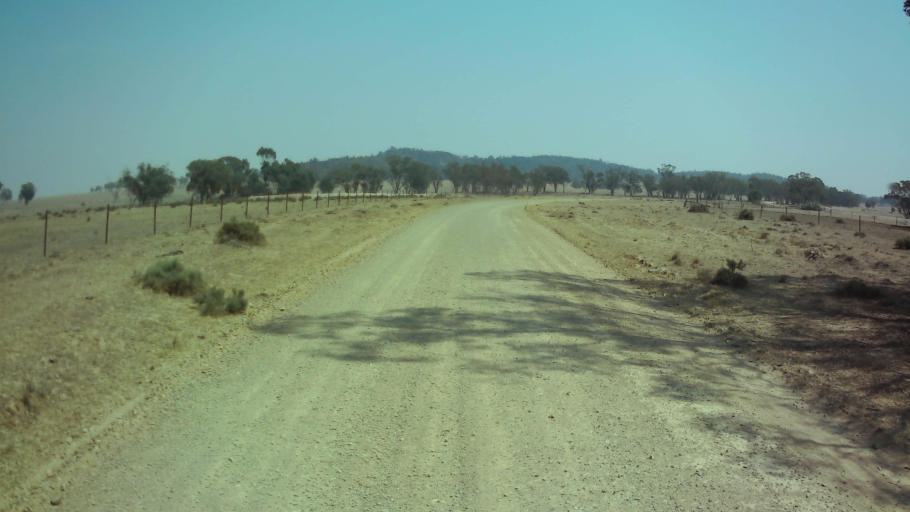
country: AU
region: New South Wales
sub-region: Weddin
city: Grenfell
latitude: -33.6766
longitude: 148.2760
